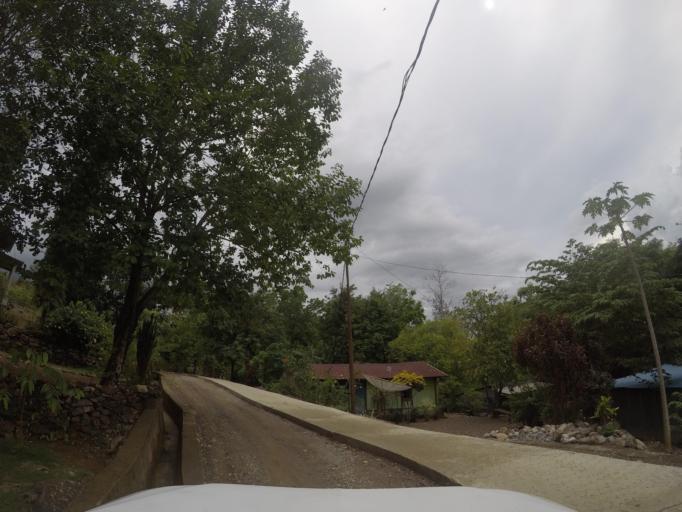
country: TL
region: Bobonaro
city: Maliana
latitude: -8.9951
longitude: 125.2148
